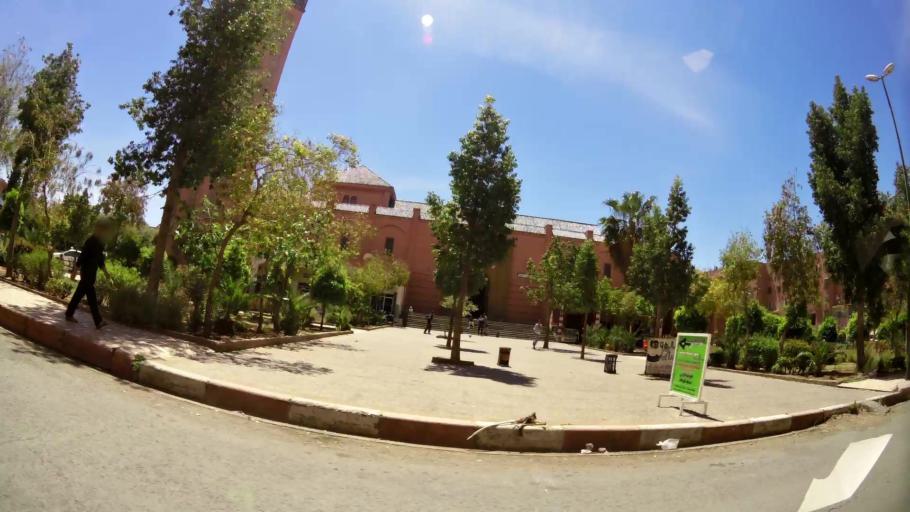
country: MA
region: Marrakech-Tensift-Al Haouz
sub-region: Marrakech
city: Marrakesh
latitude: 31.6346
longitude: -8.0558
